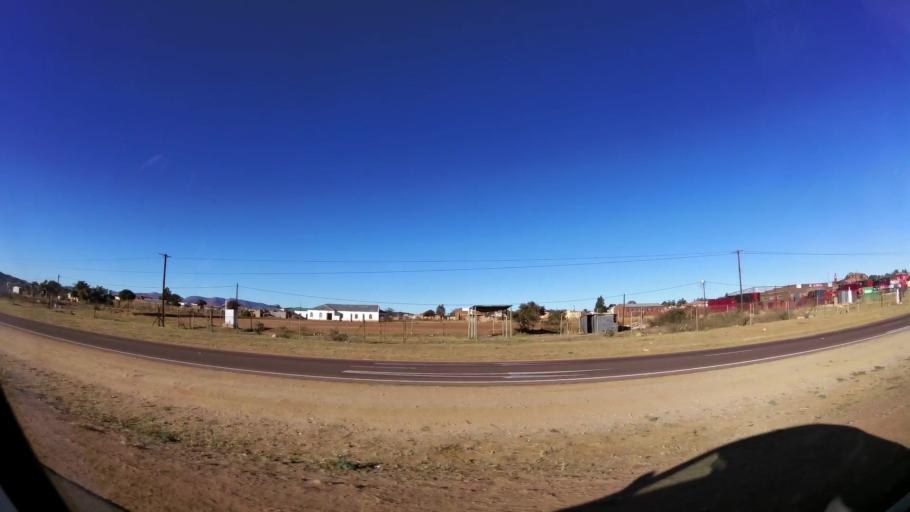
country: ZA
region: Limpopo
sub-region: Capricorn District Municipality
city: Mankoeng
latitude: -23.9111
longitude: 29.7782
